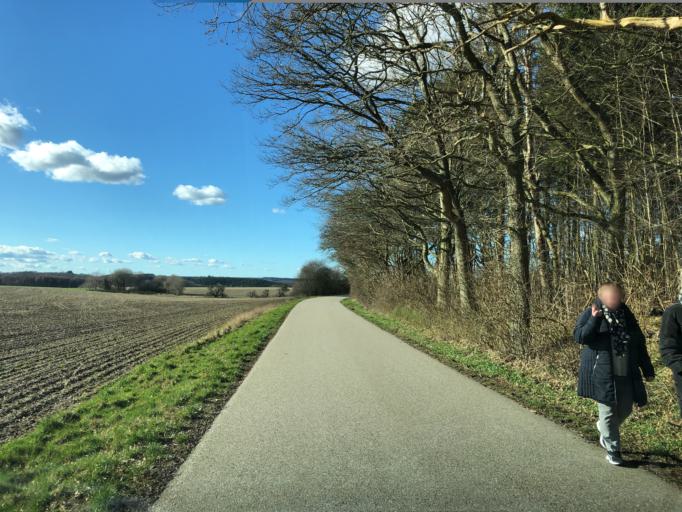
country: DK
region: Central Jutland
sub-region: Favrskov Kommune
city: Hammel
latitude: 56.3009
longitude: 9.9211
